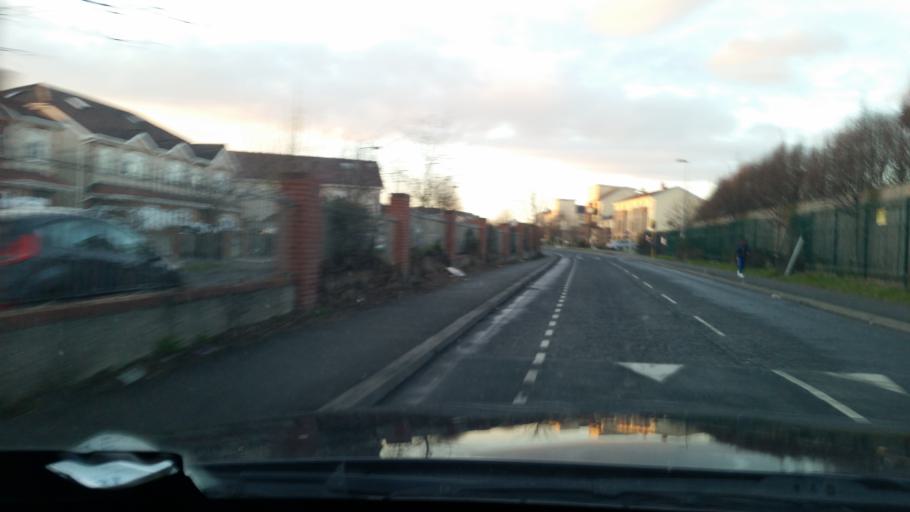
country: IE
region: Leinster
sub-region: Dublin City
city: Finglas
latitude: 53.4034
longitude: -6.2915
